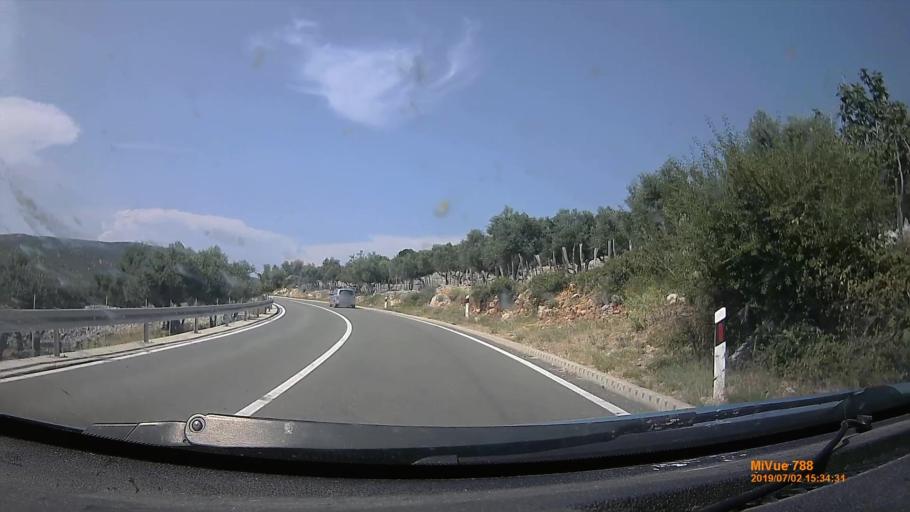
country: HR
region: Primorsko-Goranska
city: Cres
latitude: 44.9679
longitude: 14.4128
